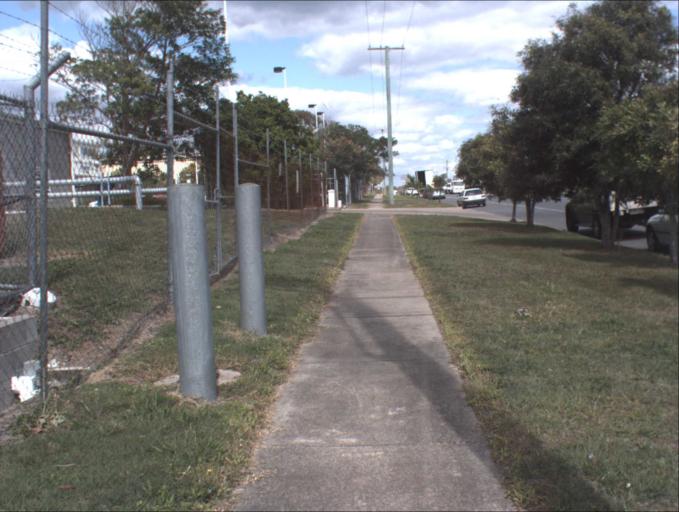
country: AU
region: Queensland
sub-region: Logan
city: Logan Reserve
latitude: -27.6814
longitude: 153.0709
